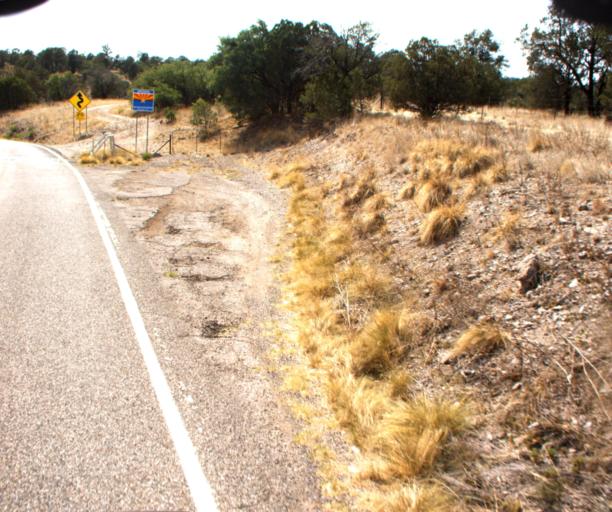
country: US
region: Arizona
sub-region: Greenlee County
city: Clifton
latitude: 33.1074
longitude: -109.0473
